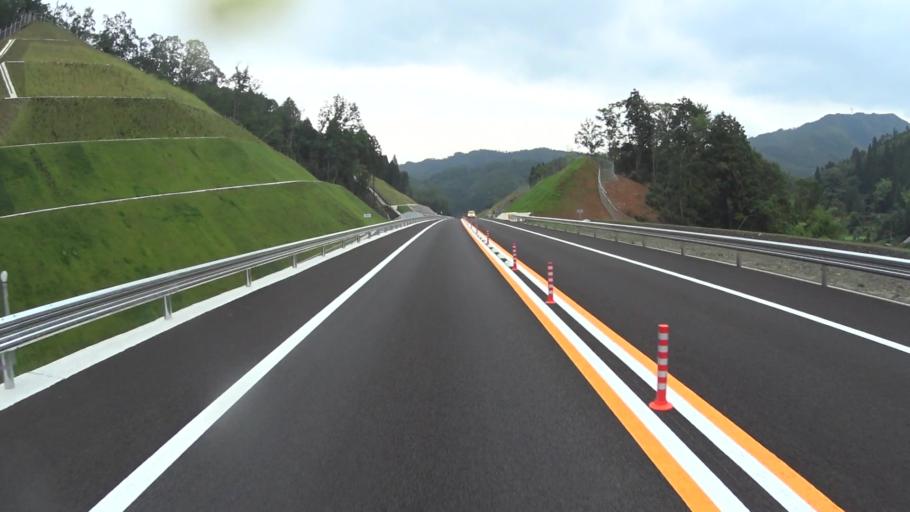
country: JP
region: Kyoto
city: Ayabe
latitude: 35.2252
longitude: 135.3444
